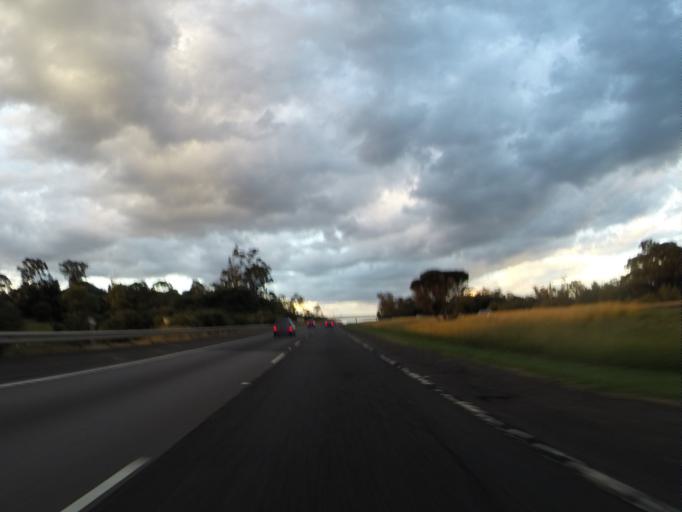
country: AU
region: New South Wales
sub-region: Campbelltown Municipality
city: Glen Alpine
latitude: -34.0913
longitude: 150.7667
